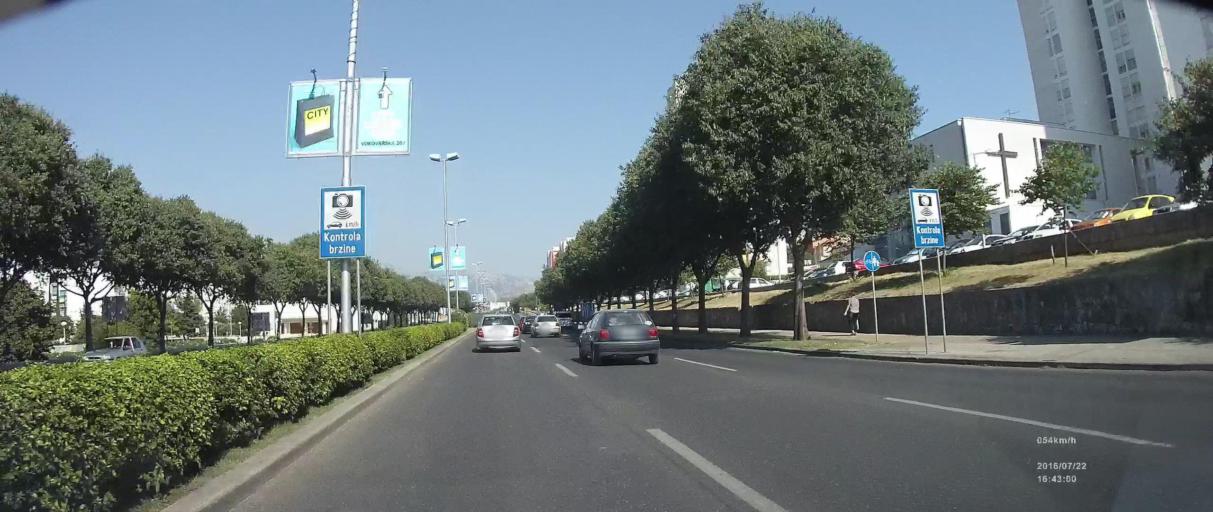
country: HR
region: Splitsko-Dalmatinska
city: Vranjic
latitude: 43.5199
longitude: 16.4631
